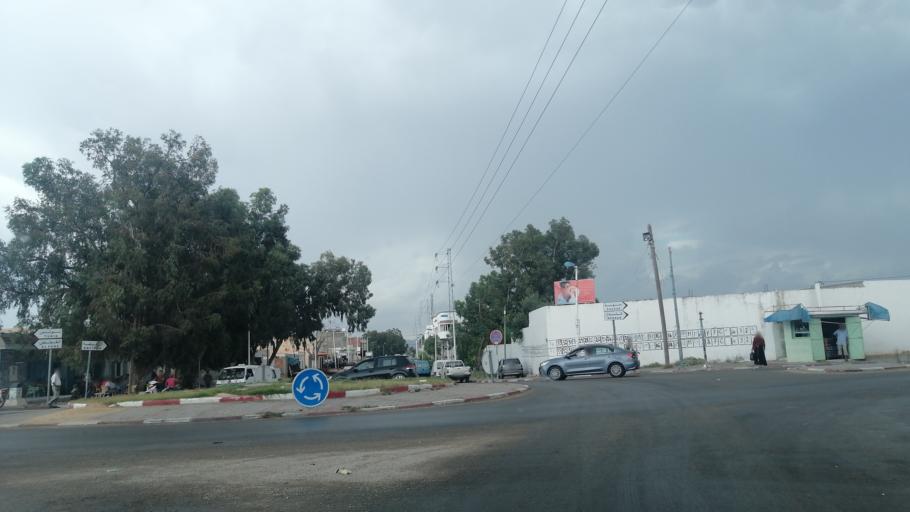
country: TN
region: Al Qayrawan
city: Sbikha
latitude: 36.1236
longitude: 10.0928
